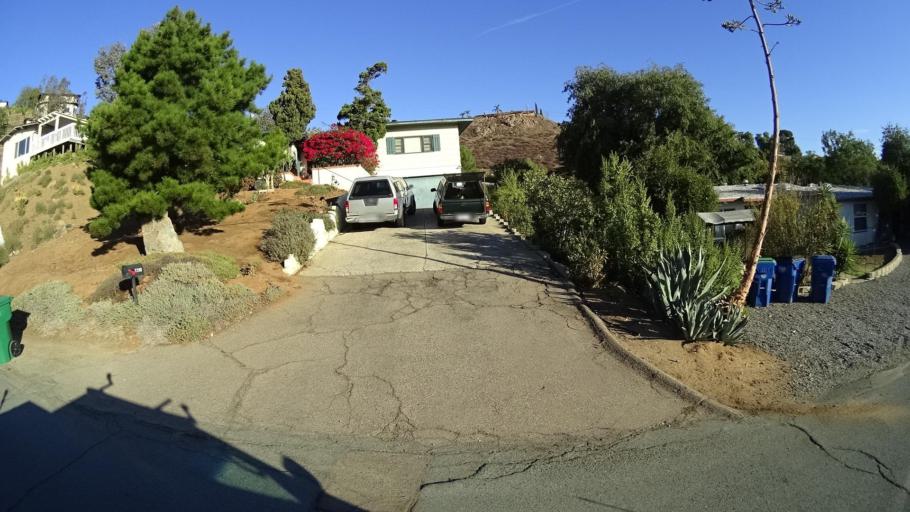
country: US
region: California
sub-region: San Diego County
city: Bostonia
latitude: 32.8164
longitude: -116.9406
